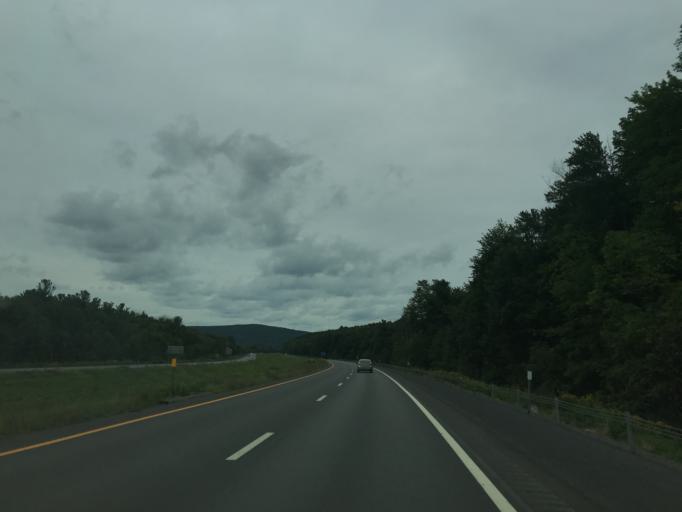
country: US
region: New York
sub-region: Delaware County
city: Sidney
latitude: 42.2960
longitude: -75.3855
